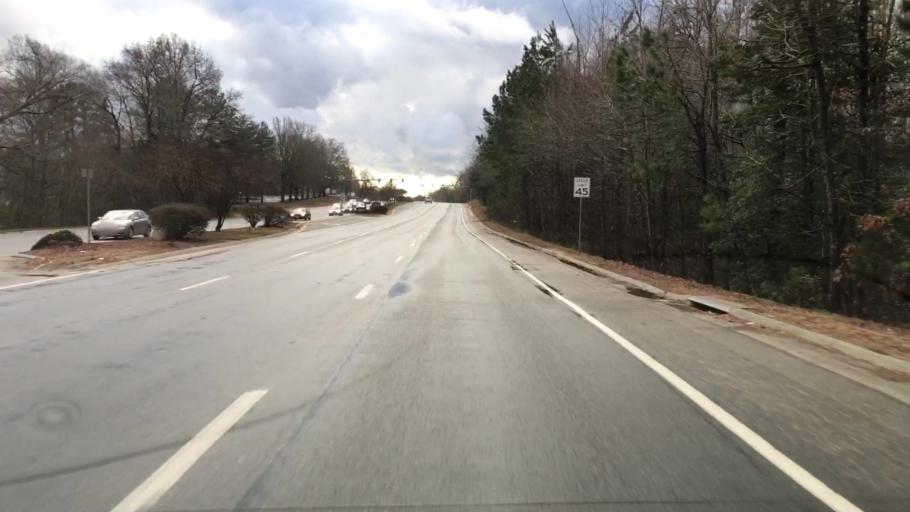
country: US
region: Virginia
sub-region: Chesterfield County
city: Bon Air
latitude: 37.5016
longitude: -77.6098
